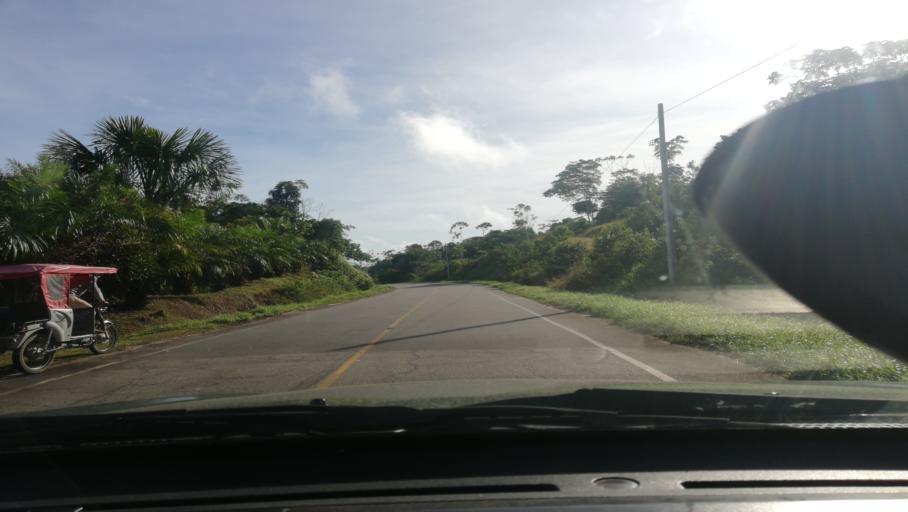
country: PE
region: Loreto
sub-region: Provincia de Loreto
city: Nauta
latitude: -4.3679
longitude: -73.5599
